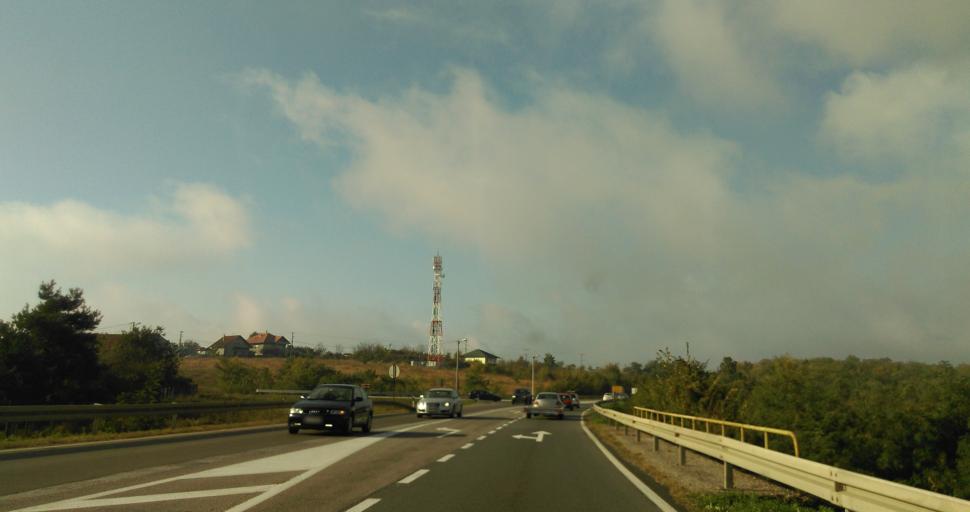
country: RS
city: Rusanj
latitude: 44.6519
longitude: 20.4299
